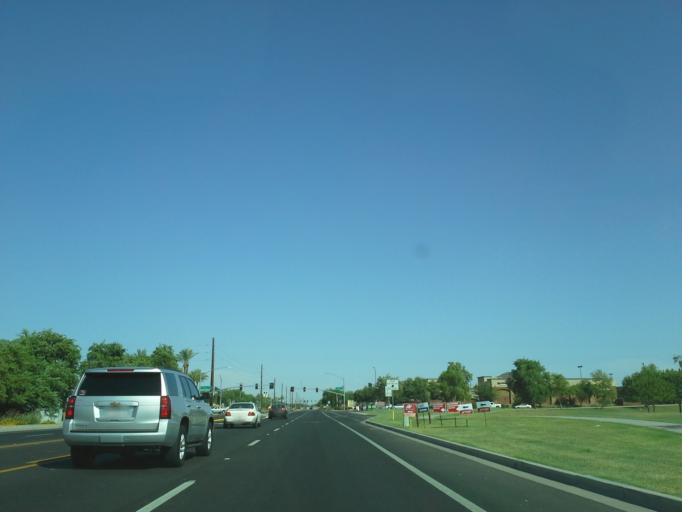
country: US
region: Arizona
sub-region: Pinal County
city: San Tan Valley
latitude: 33.1809
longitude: -111.5866
